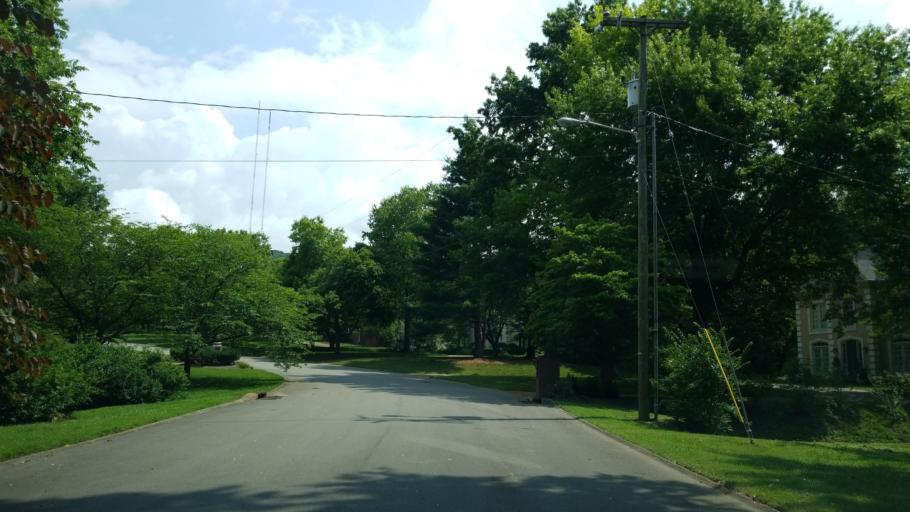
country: US
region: Tennessee
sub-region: Davidson County
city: Forest Hills
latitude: 36.0382
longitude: -86.8363
